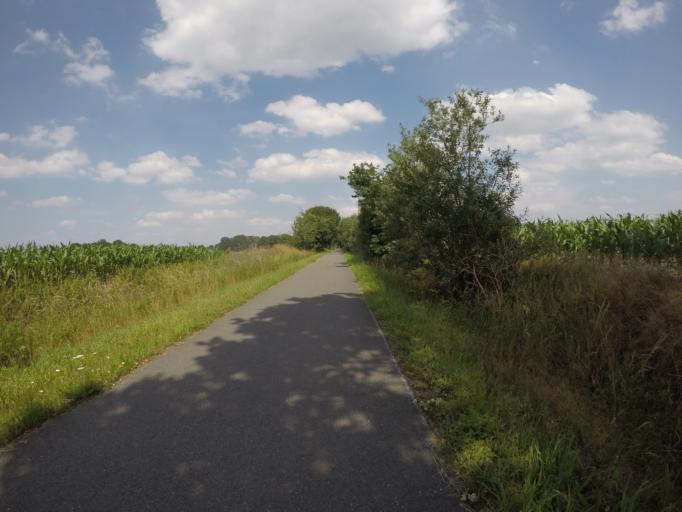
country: DE
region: North Rhine-Westphalia
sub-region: Regierungsbezirk Munster
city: Borken
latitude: 51.8401
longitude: 6.8237
